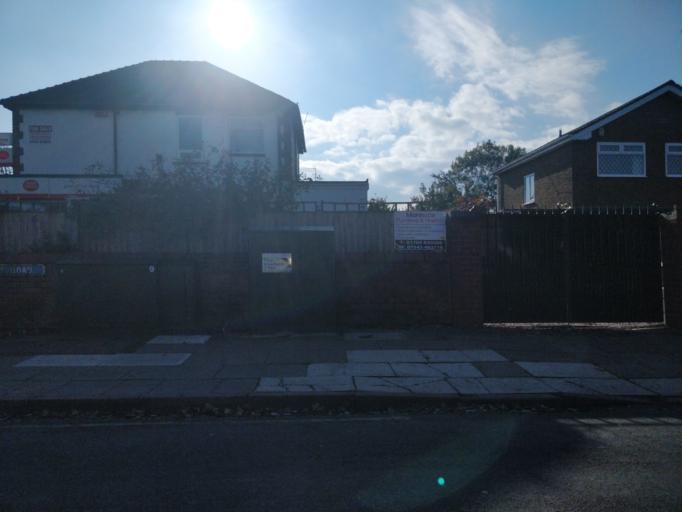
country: GB
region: England
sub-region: Lancashire
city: Banks
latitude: 53.6703
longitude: -2.9578
